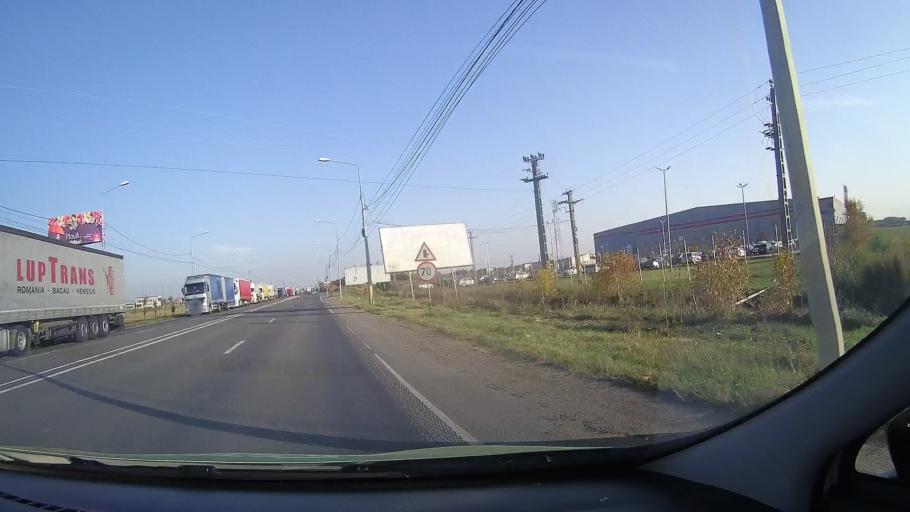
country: RO
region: Bihor
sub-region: Comuna Bors
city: Bors
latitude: 47.1075
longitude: 21.8238
